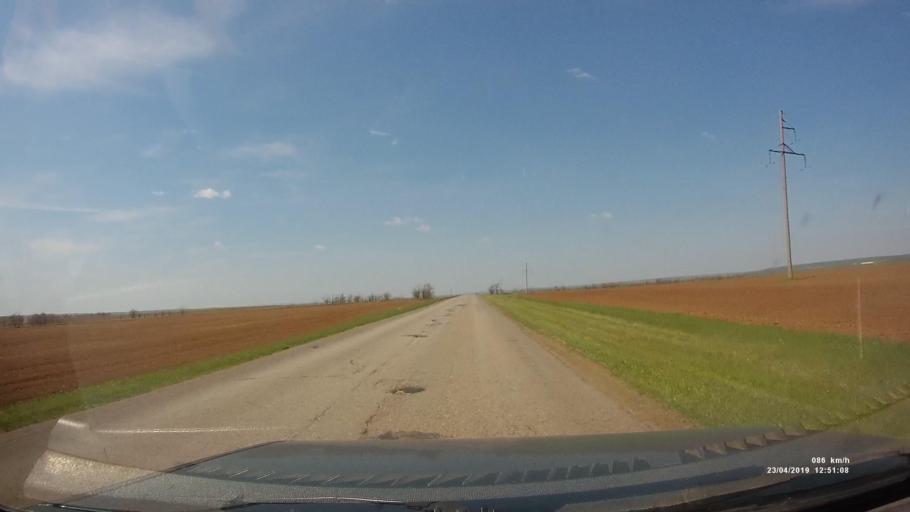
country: RU
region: Kalmykiya
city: Yashalta
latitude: 46.5520
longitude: 42.6267
